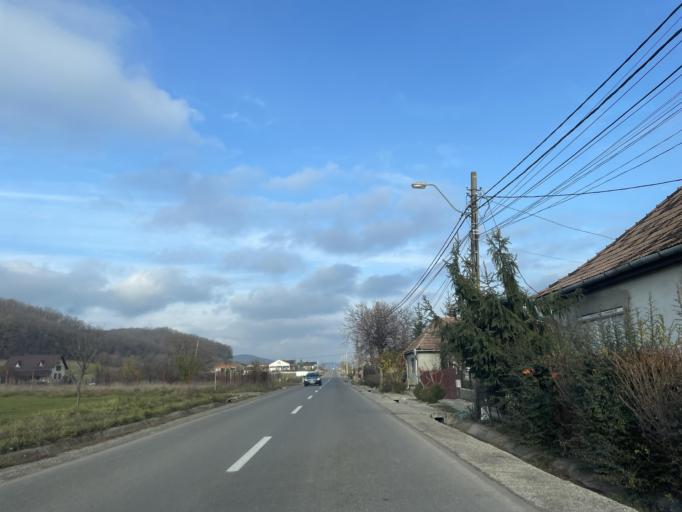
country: RO
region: Mures
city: Reghin-Sat
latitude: 46.7914
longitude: 24.7038
